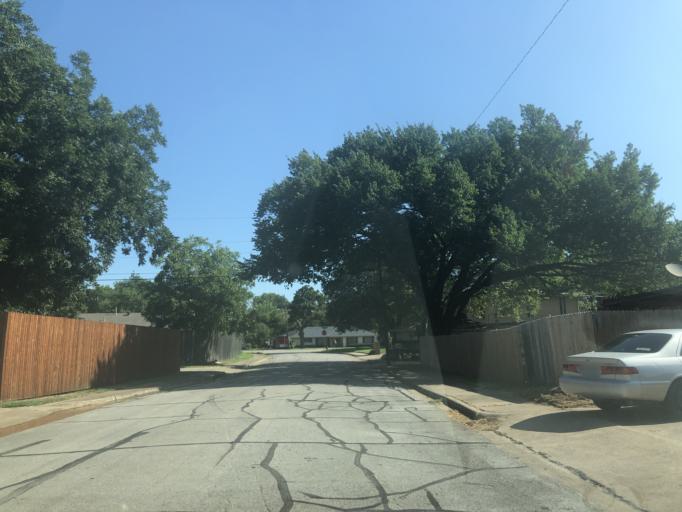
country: US
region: Texas
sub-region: Dallas County
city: Grand Prairie
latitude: 32.7626
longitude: -97.0176
